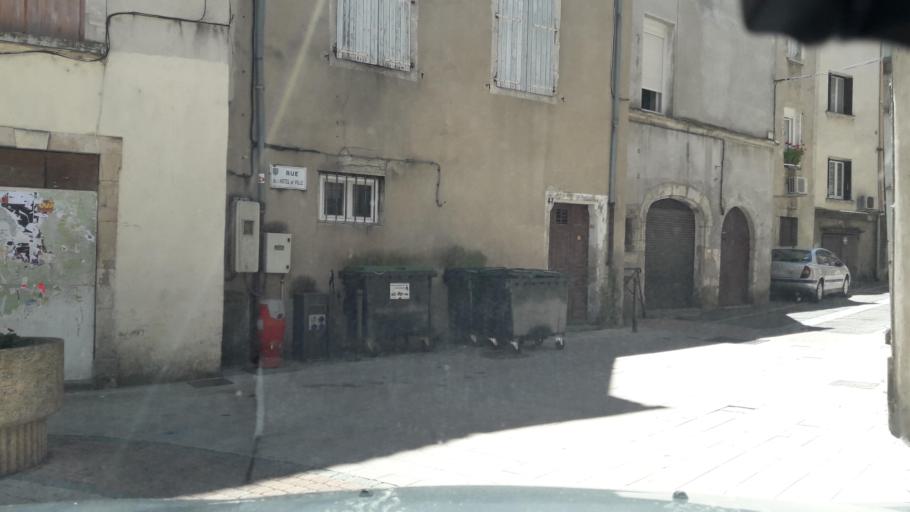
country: FR
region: Languedoc-Roussillon
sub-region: Departement du Gard
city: Saint-Ambroix
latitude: 44.2611
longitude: 4.1980
